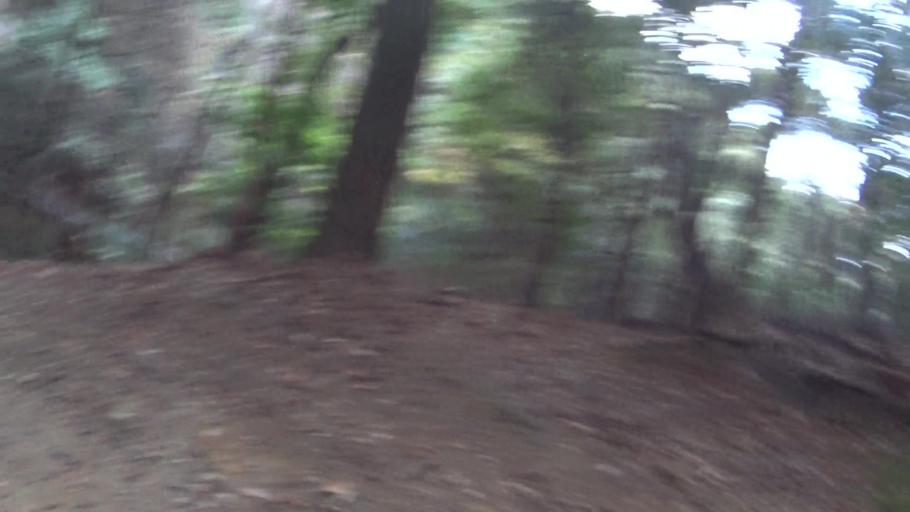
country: JP
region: Kyoto
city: Uji
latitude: 34.9506
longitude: 135.8281
